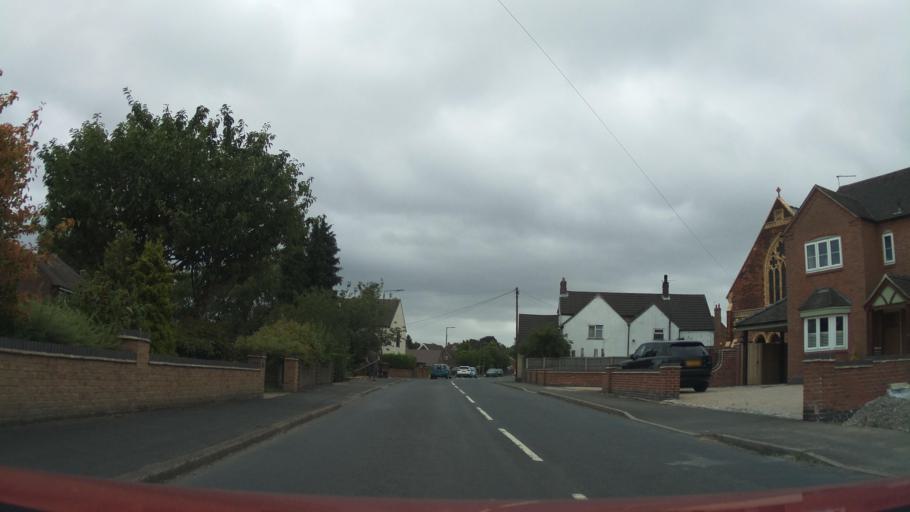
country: GB
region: England
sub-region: Derbyshire
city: Swadlincote
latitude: 52.7878
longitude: -1.5228
